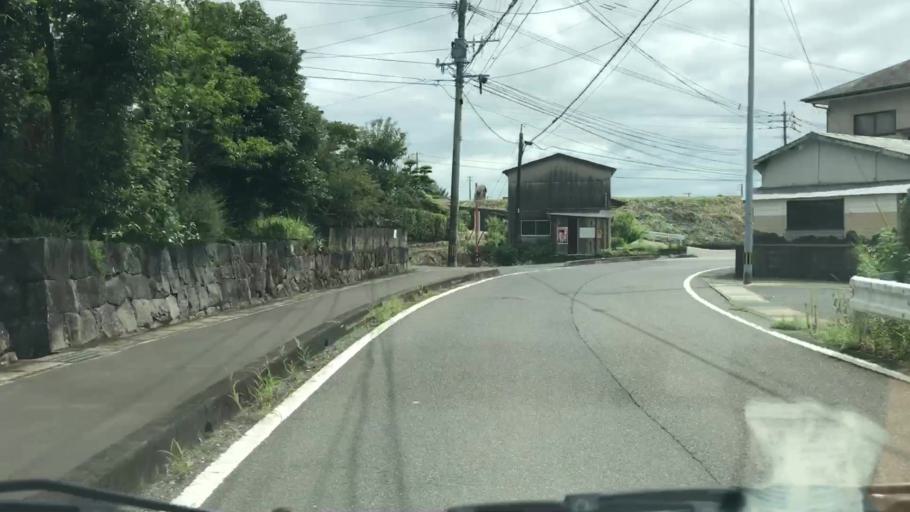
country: JP
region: Saga Prefecture
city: Kashima
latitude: 33.2238
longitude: 130.1569
